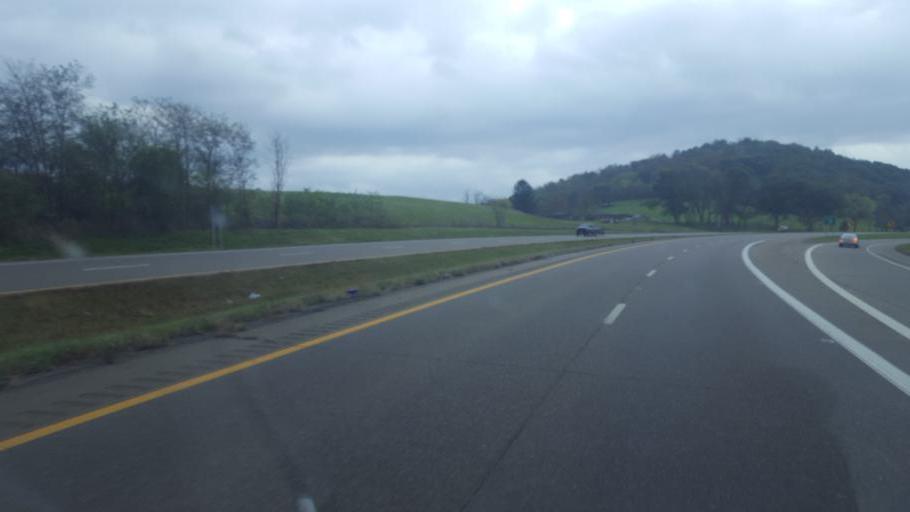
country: US
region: Ohio
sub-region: Tuscarawas County
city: New Philadelphia
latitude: 40.4562
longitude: -81.4003
